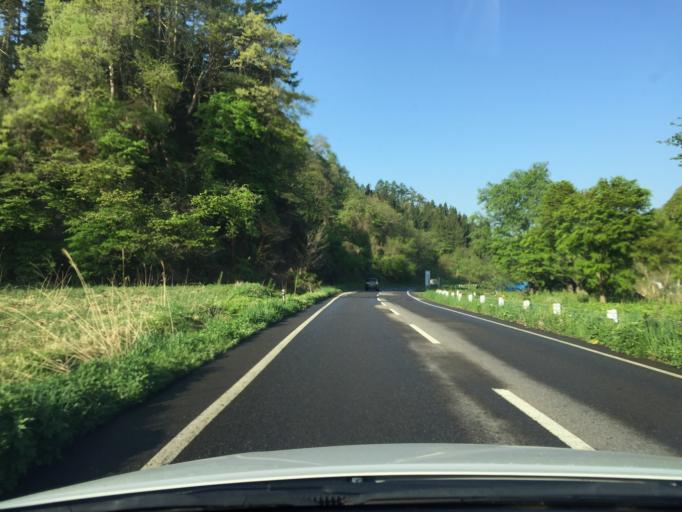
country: JP
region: Fukushima
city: Kitakata
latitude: 37.6659
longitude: 139.9680
